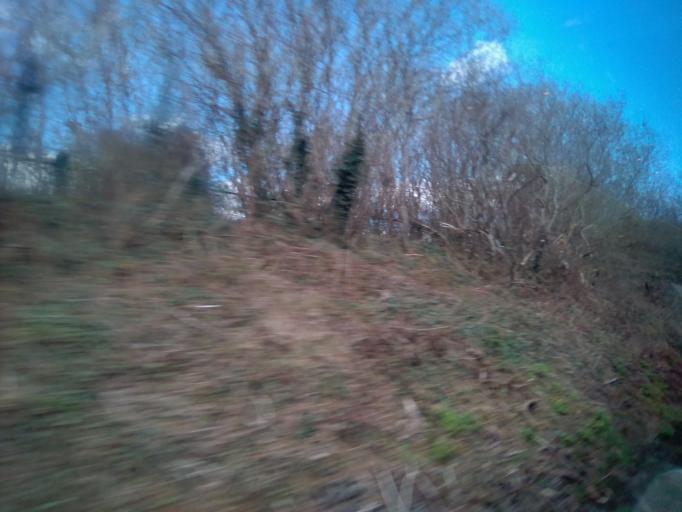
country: IE
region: Munster
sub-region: County Cork
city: Millstreet
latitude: 52.0847
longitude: -9.2062
